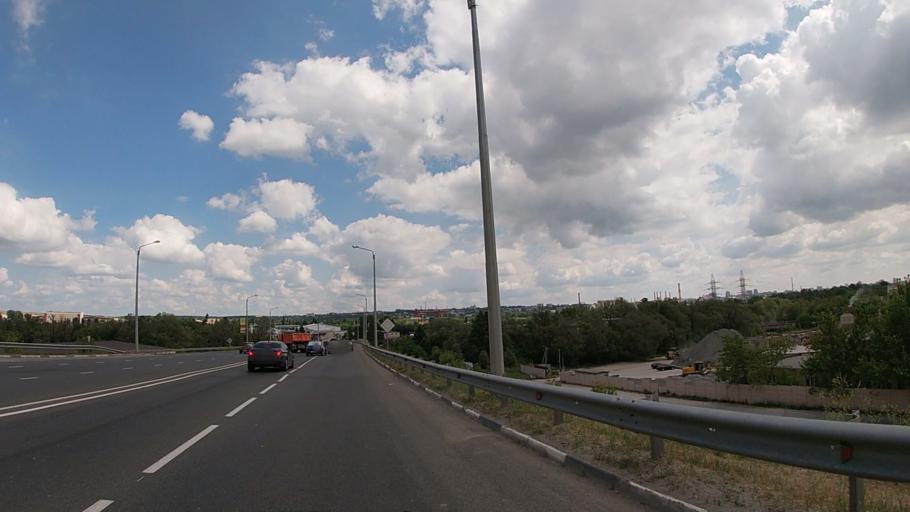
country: RU
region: Belgorod
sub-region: Belgorodskiy Rayon
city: Belgorod
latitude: 50.6065
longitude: 36.5315
